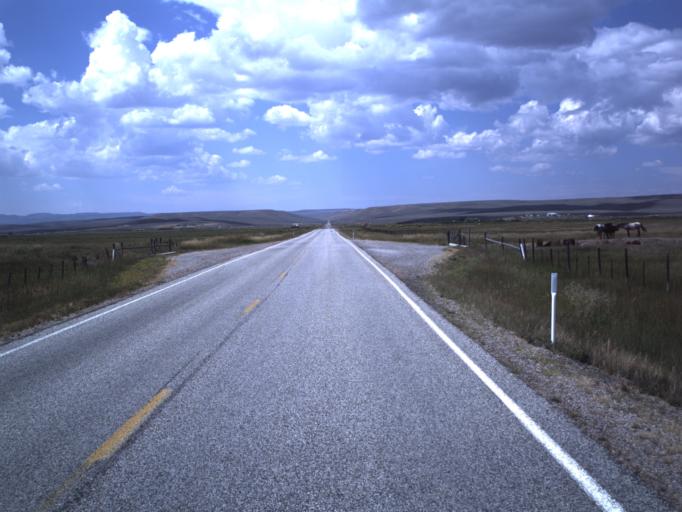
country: US
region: Utah
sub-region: Rich County
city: Randolph
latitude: 41.7755
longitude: -111.0904
